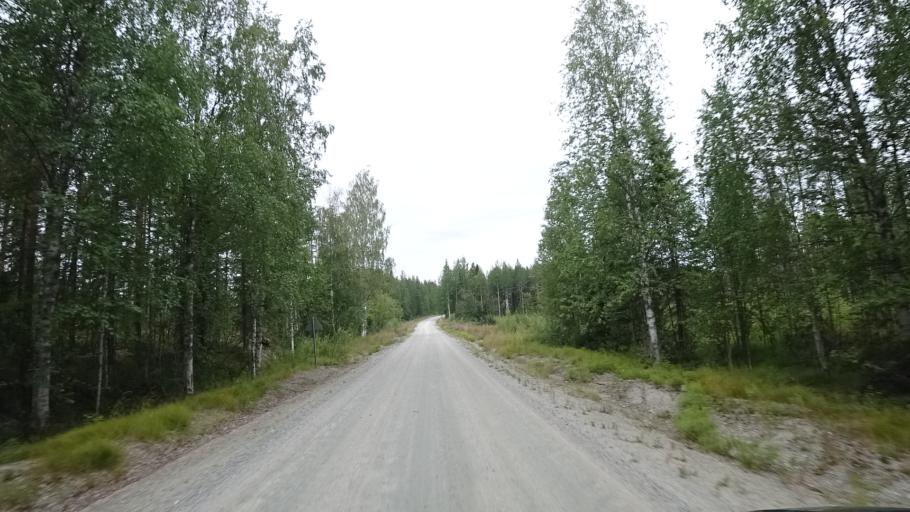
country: FI
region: North Karelia
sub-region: Joensuu
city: Ilomantsi
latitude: 63.1541
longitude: 30.6182
